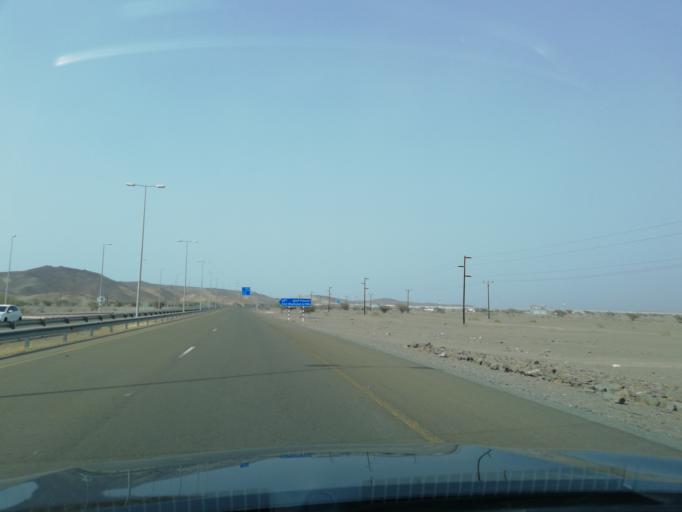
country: OM
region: Al Batinah
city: Al Liwa'
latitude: 24.3718
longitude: 56.5361
